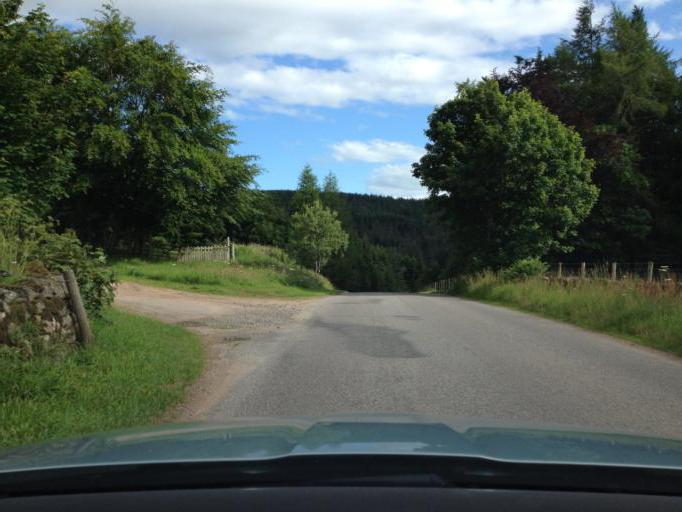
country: GB
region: Scotland
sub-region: Aberdeenshire
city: Banchory
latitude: 56.9669
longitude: -2.5761
